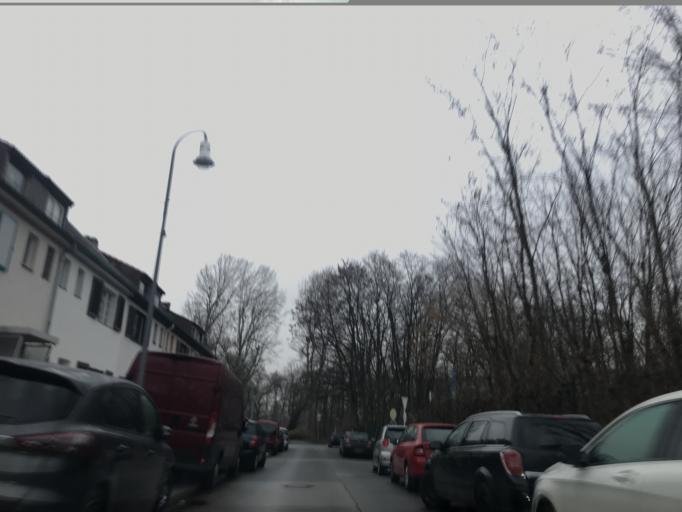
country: DE
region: Berlin
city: Haselhorst
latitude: 52.5462
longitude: 13.2432
